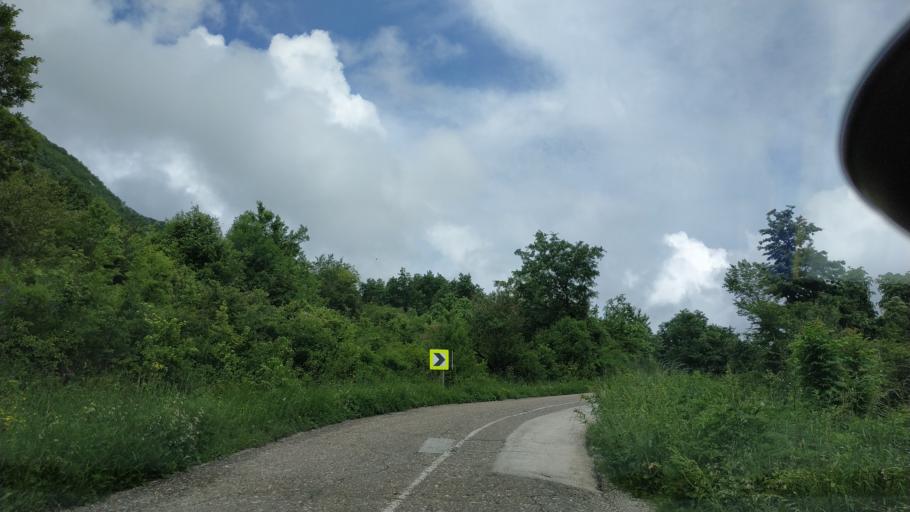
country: RS
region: Central Serbia
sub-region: Zajecarski Okrug
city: Boljevac
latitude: 43.7432
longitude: 21.9482
